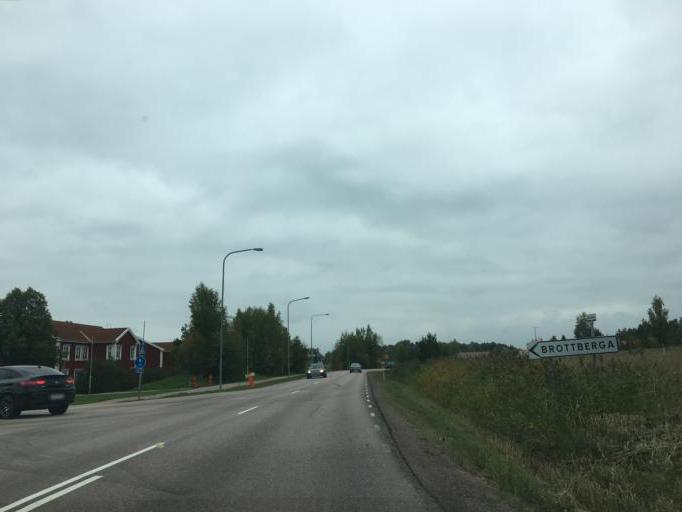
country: SE
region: Vaestmanland
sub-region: Vasteras
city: Vasteras
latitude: 59.6317
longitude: 16.4962
